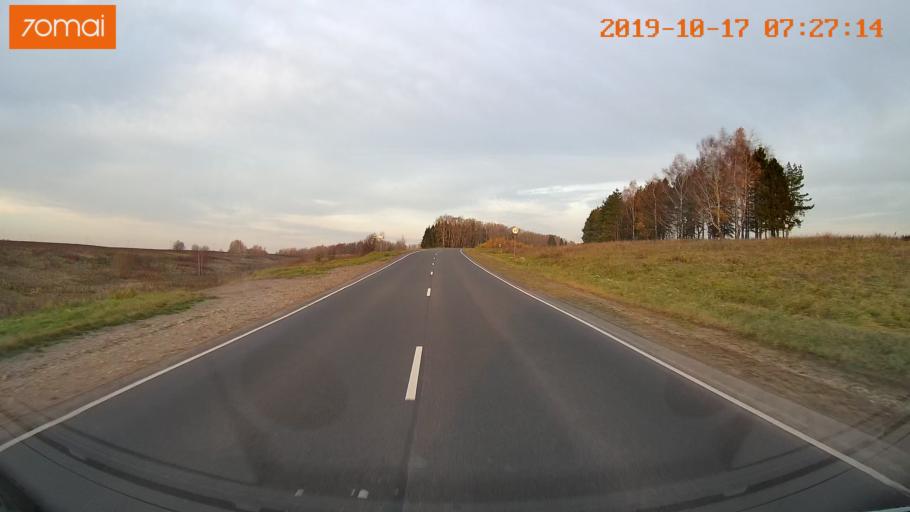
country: RU
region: Ivanovo
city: Gavrilov Posad
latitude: 56.3608
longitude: 40.0809
